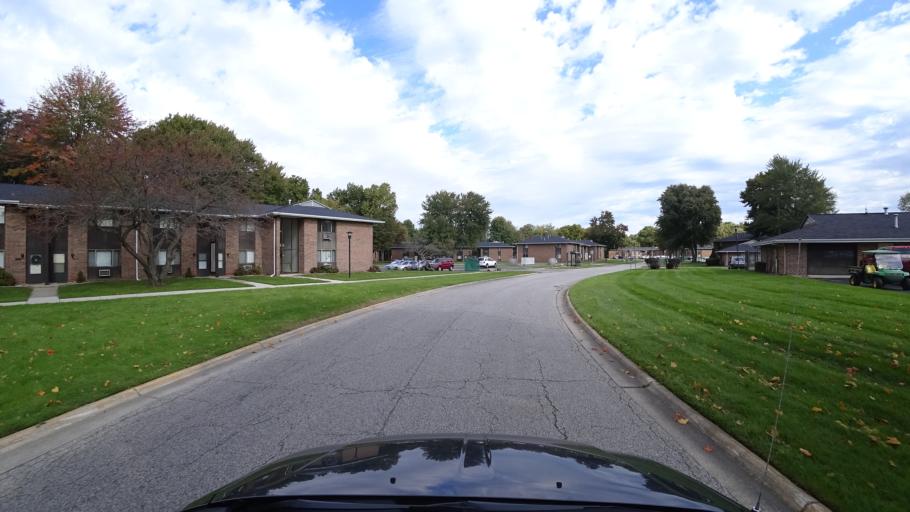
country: US
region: Indiana
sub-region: LaPorte County
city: Trail Creek
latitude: 41.6924
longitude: -86.8690
